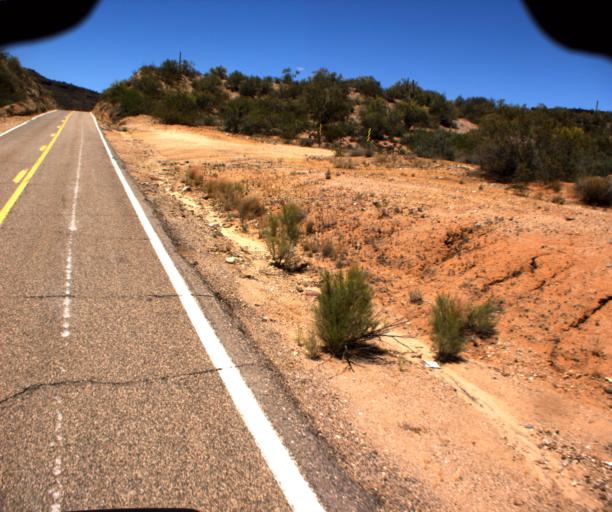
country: US
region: Arizona
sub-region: Yavapai County
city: Bagdad
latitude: 34.4816
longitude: -113.0614
